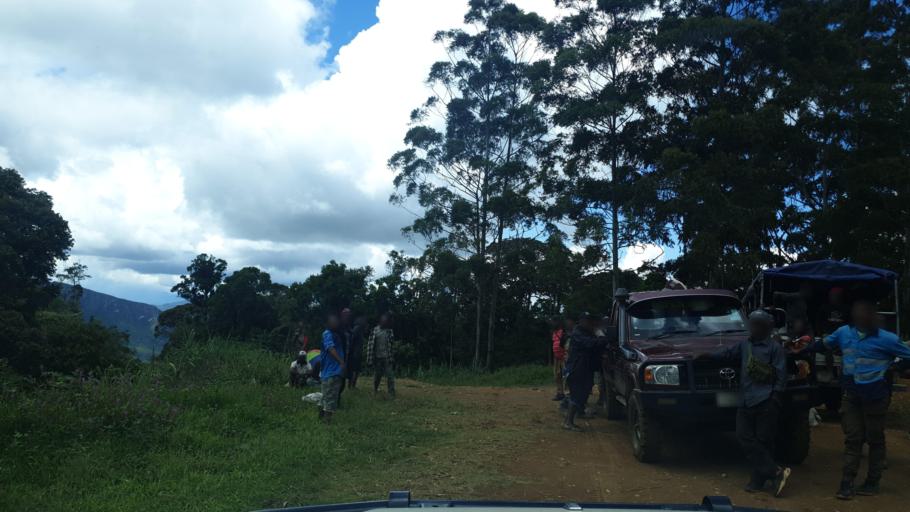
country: PG
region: Eastern Highlands
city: Goroka
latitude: -6.2787
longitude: 145.1987
